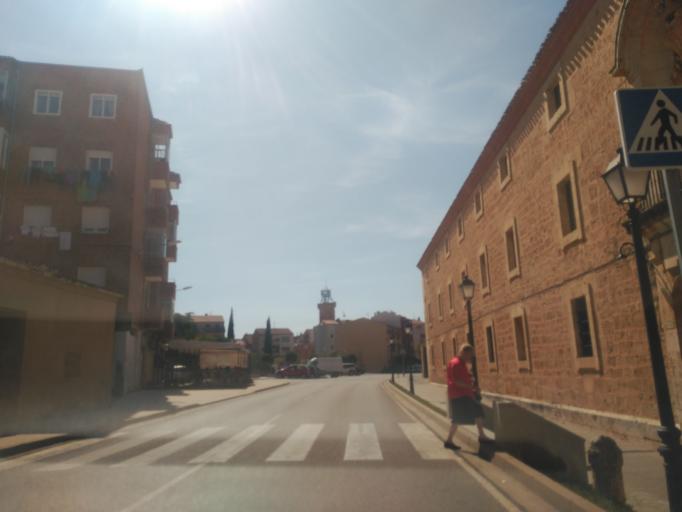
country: ES
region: Castille and Leon
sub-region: Provincia de Soria
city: El Burgo de Osma
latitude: 41.5903
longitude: -3.0633
